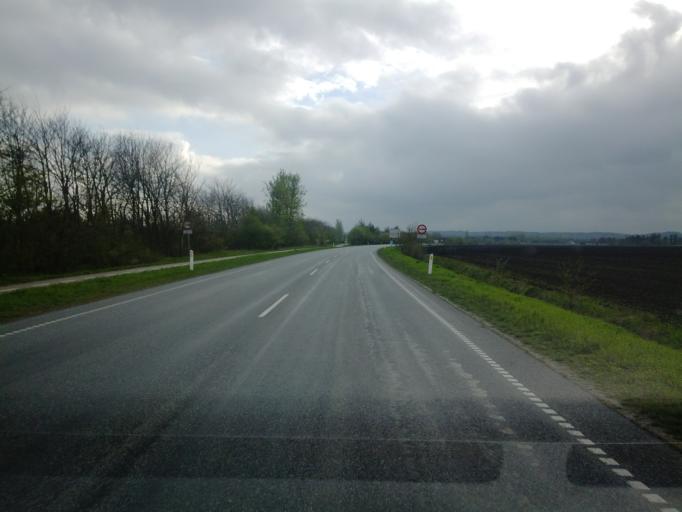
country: DK
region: North Denmark
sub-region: Bronderslev Kommune
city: Dronninglund
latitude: 57.2578
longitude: 10.3100
